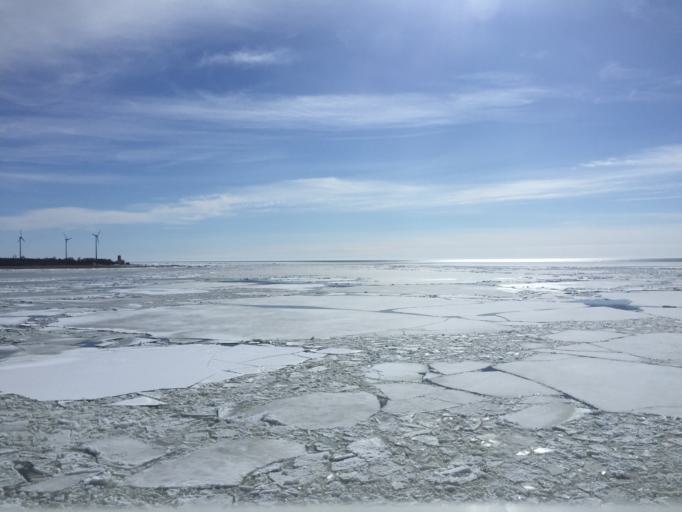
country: EE
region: Laeaene
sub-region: Lihula vald
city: Lihula
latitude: 58.5765
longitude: 23.4943
